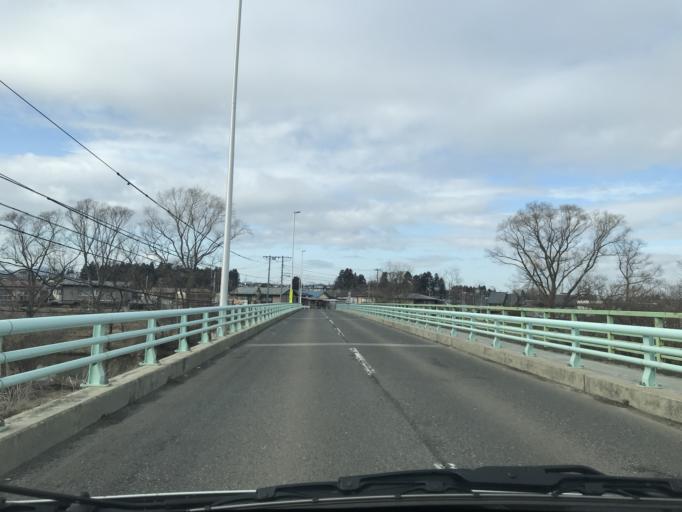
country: JP
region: Iwate
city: Hanamaki
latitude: 39.3785
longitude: 141.1066
